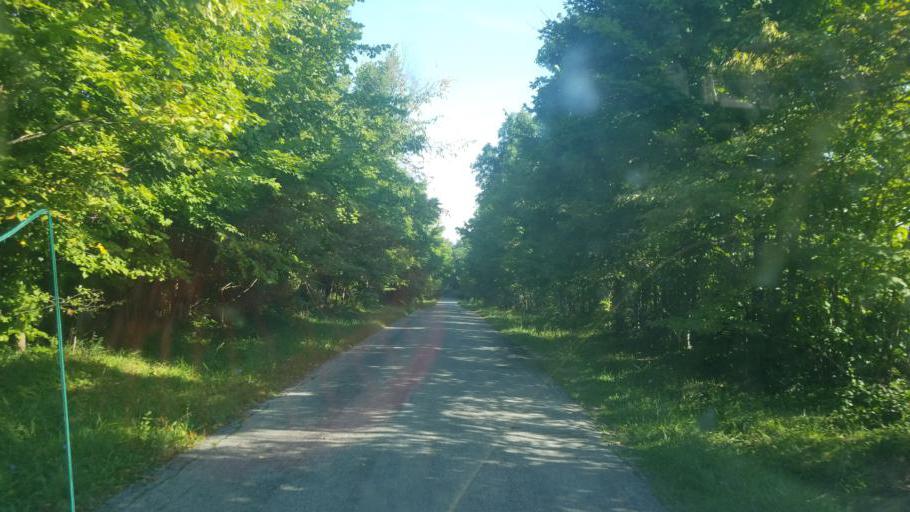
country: US
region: Ohio
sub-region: Lorain County
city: Wellington
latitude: 41.0666
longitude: -82.2797
